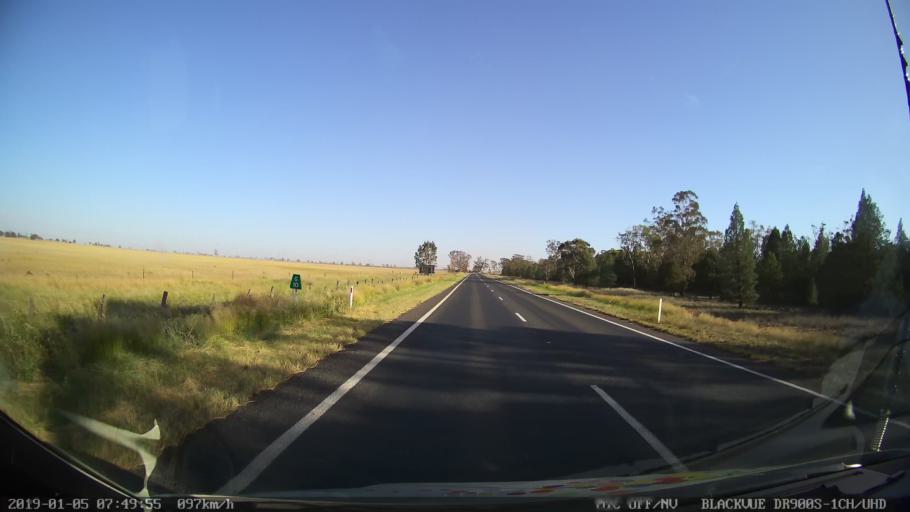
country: AU
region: New South Wales
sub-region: Gilgandra
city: Gilgandra
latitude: -31.7946
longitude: 148.6358
